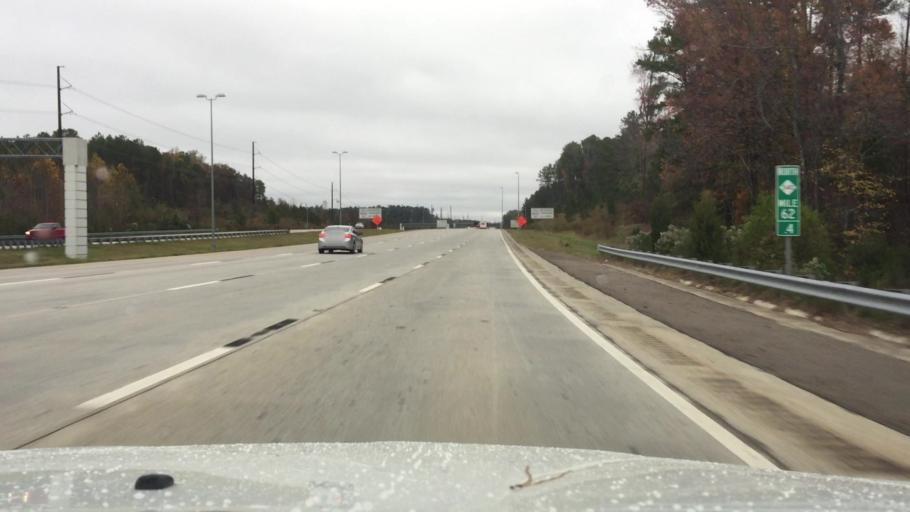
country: US
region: North Carolina
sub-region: Wake County
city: Green Level
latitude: 35.7875
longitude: -78.8871
